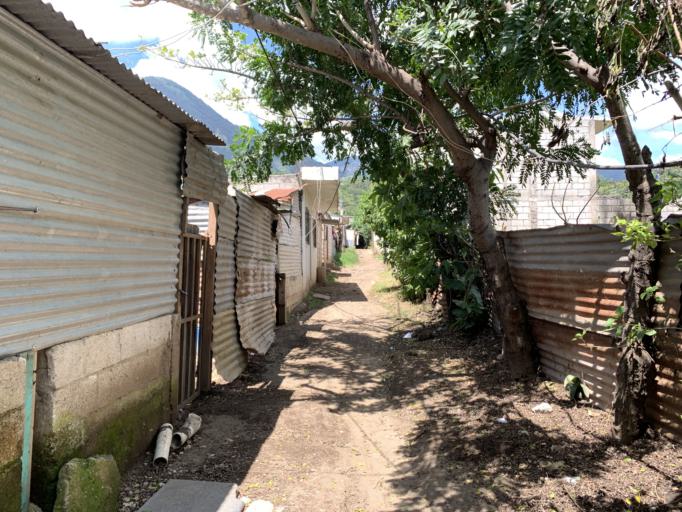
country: GT
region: Guatemala
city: Amatitlan
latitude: 14.4873
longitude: -90.6426
